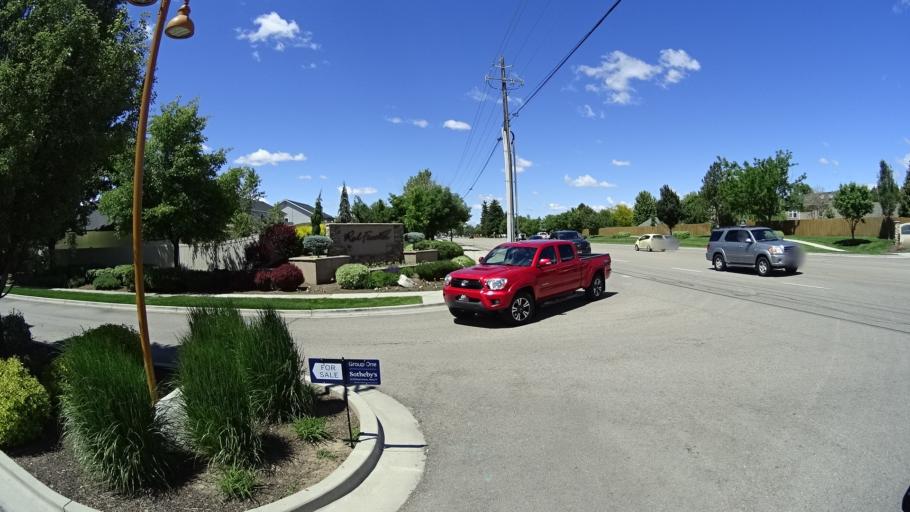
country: US
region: Idaho
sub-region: Ada County
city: Meridian
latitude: 43.6337
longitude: -116.3429
